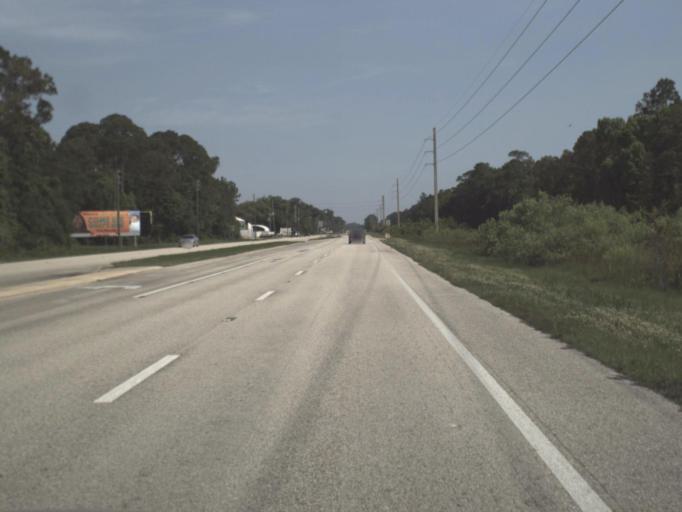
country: US
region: Florida
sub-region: Saint Johns County
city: Villano Beach
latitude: 29.9848
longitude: -81.3673
